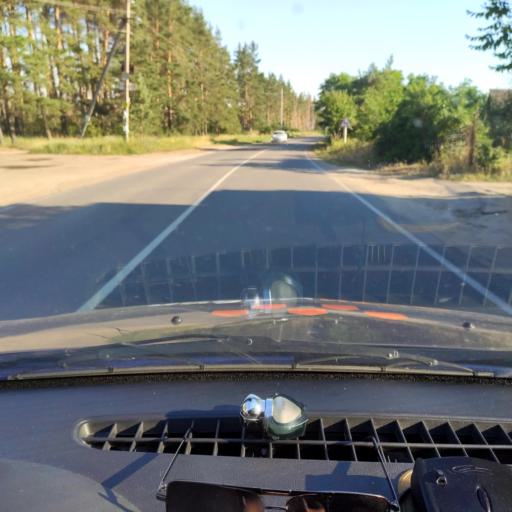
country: RU
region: Voronezj
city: Podgornoye
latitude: 51.8378
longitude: 39.1437
